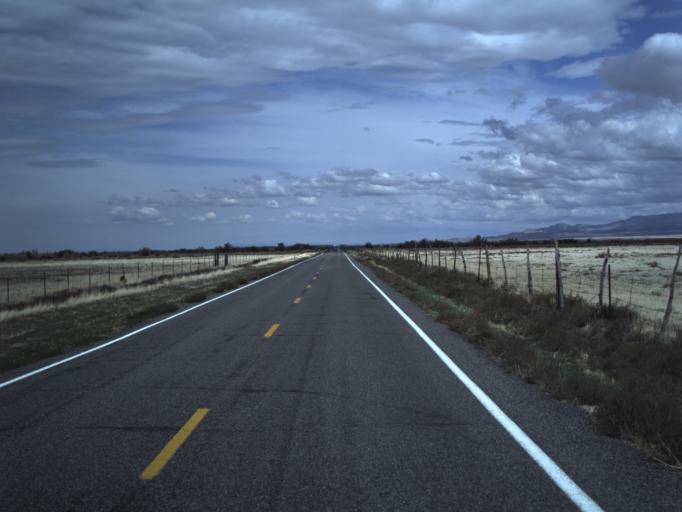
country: US
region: Utah
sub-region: Millard County
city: Fillmore
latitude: 39.0638
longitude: -112.4098
